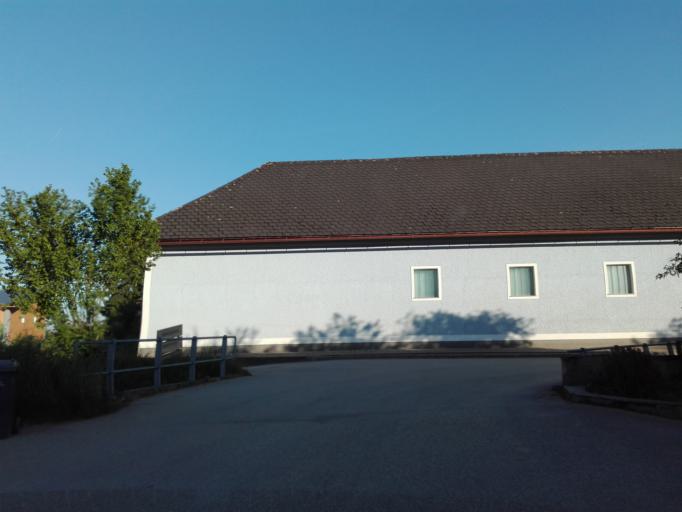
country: AT
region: Upper Austria
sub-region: Politischer Bezirk Urfahr-Umgebung
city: Feldkirchen an der Donau
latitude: 48.3231
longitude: 14.0002
